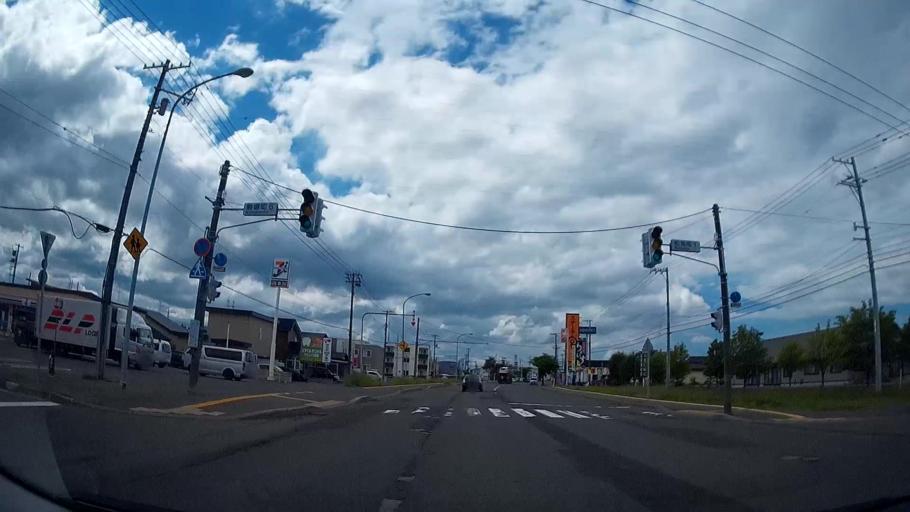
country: JP
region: Hokkaido
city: Chitose
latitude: 42.8715
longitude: 141.5868
